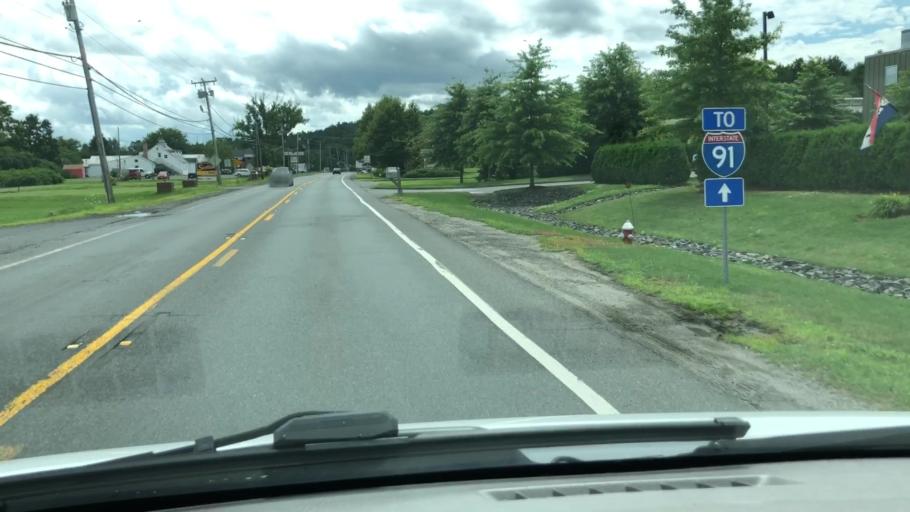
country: US
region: Massachusetts
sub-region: Hampshire County
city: Hatfield
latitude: 42.3700
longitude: -72.6363
